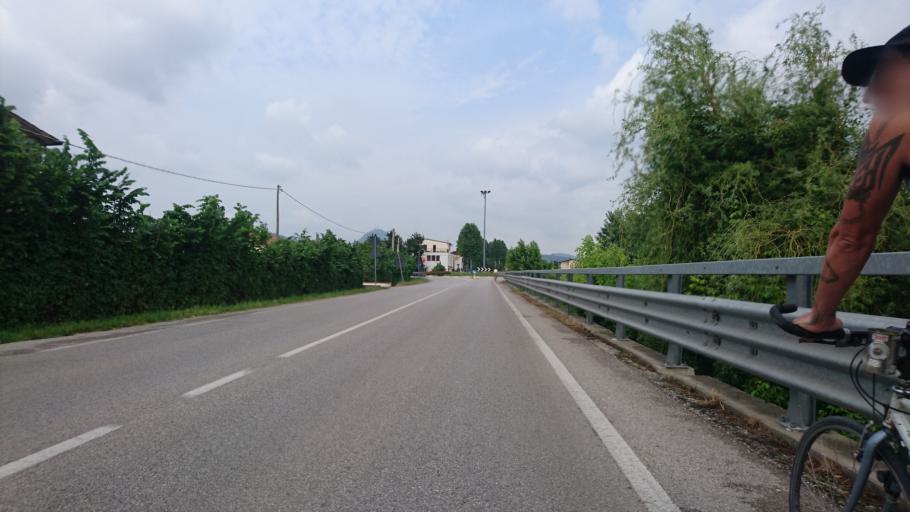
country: IT
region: Veneto
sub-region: Provincia di Padova
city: Monselice
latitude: 45.2456
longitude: 11.7357
